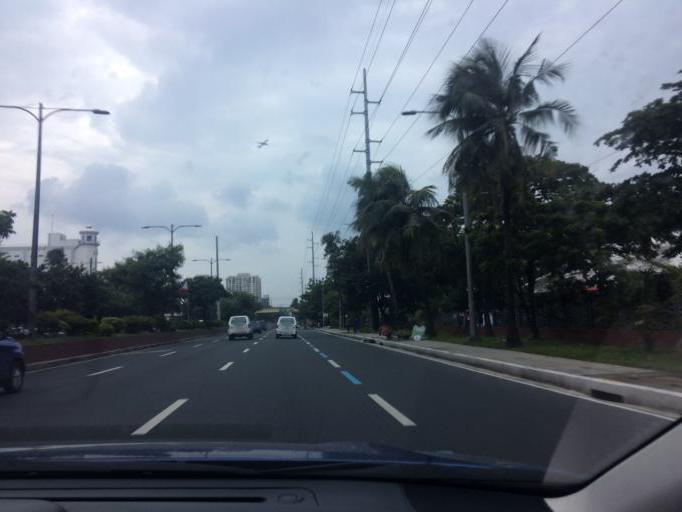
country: PH
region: Metro Manila
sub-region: Makati City
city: Makati City
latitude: 14.5476
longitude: 120.9906
